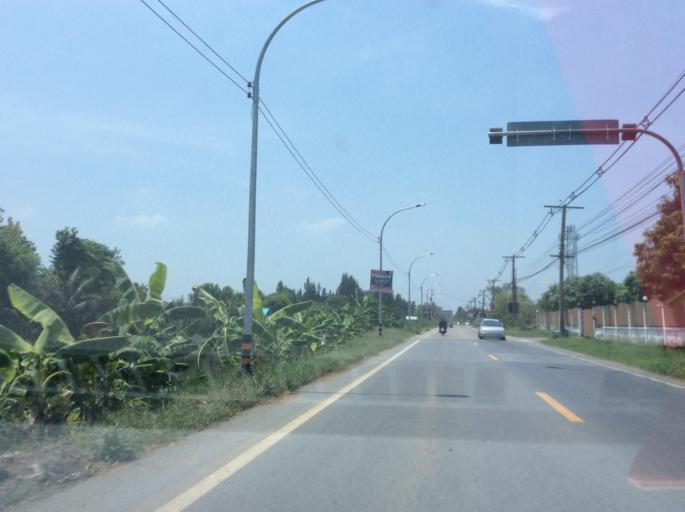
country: TH
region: Pathum Thani
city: Ban Rangsit
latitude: 14.0237
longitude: 100.7785
